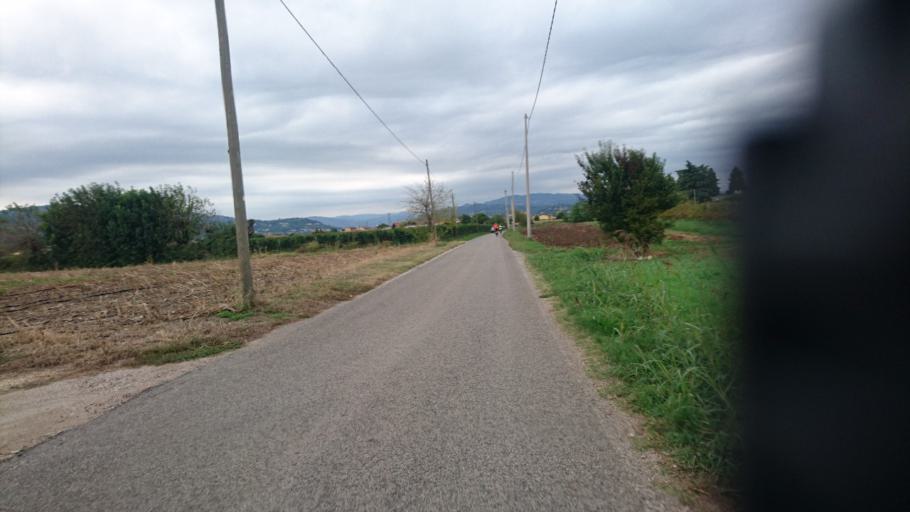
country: IT
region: Veneto
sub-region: Provincia di Vicenza
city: Zermeghedo
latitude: 45.4919
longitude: 11.3777
